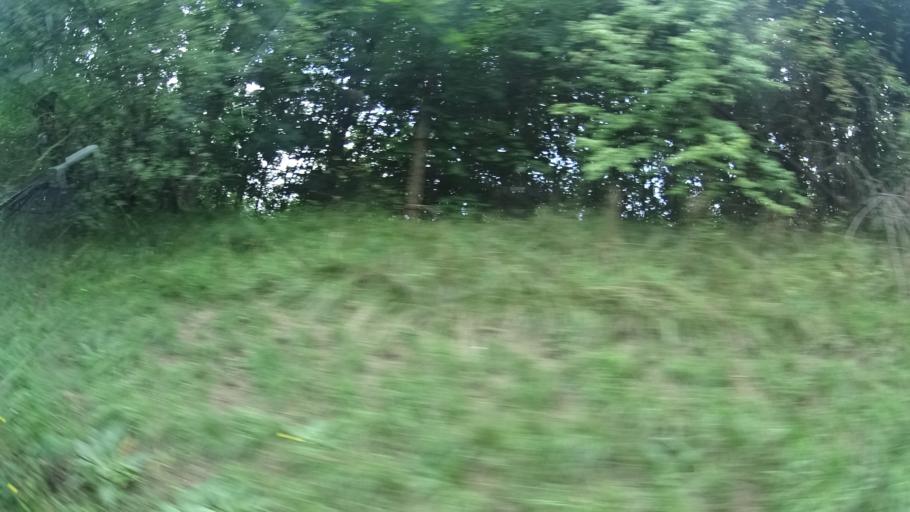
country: DE
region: Thuringia
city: Saalfeld
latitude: 50.6512
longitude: 11.3809
